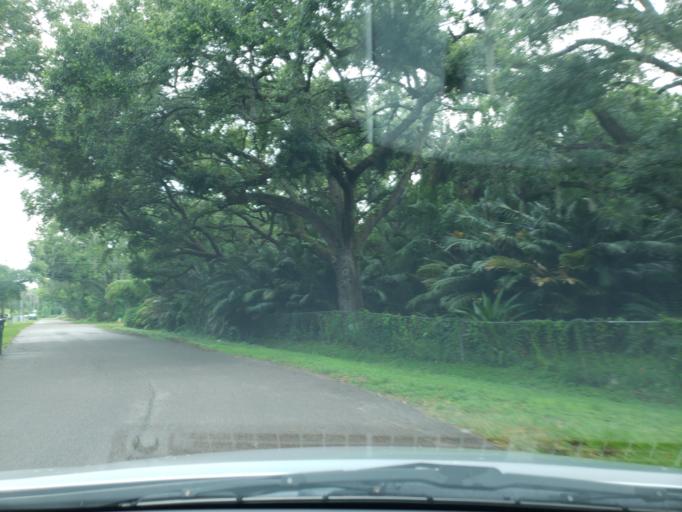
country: US
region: Florida
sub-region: Hillsborough County
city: Palm River-Clair Mel
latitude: 27.9286
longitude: -82.4051
